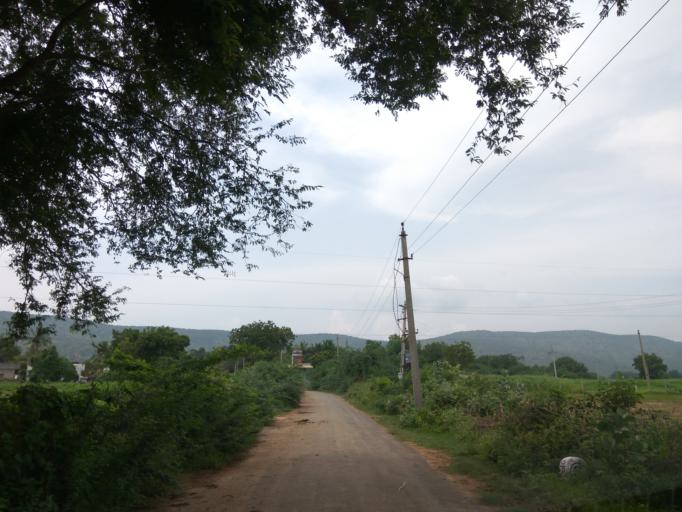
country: IN
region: Andhra Pradesh
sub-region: Prakasam
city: Cumbum
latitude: 15.4546
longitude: 79.0754
